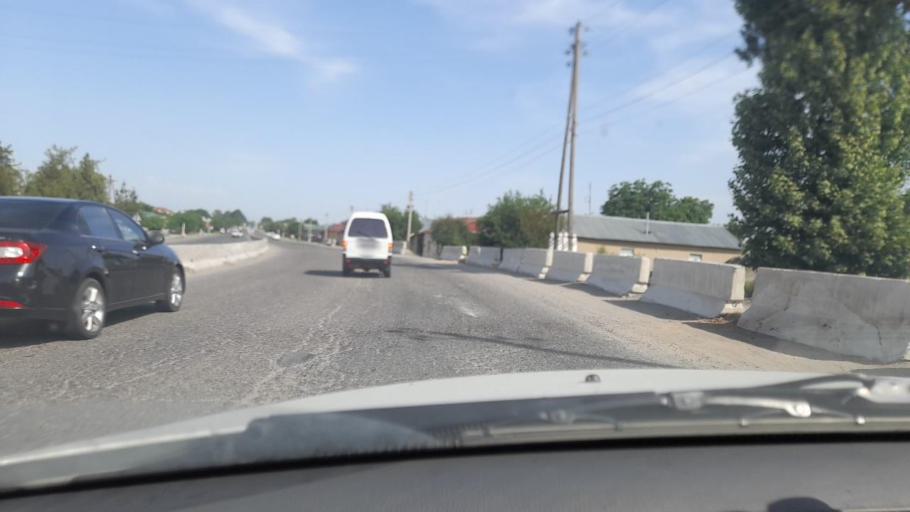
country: UZ
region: Samarqand
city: Daxbet
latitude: 39.7648
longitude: 66.9033
